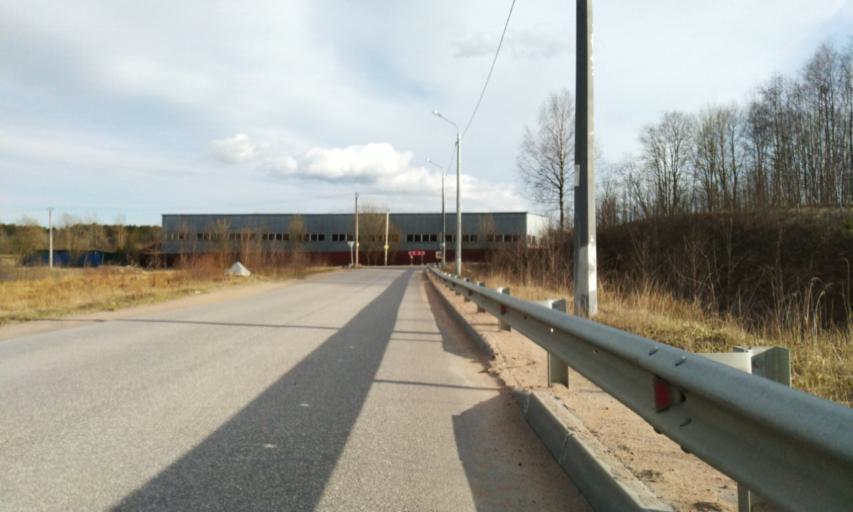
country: RU
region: Leningrad
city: Bugry
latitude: 60.1147
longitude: 30.4293
